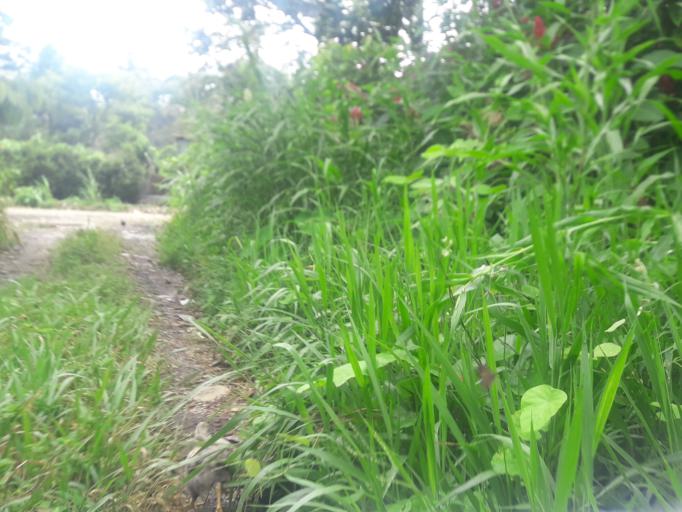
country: EC
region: Napo
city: Tena
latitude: -0.9747
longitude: -77.8473
